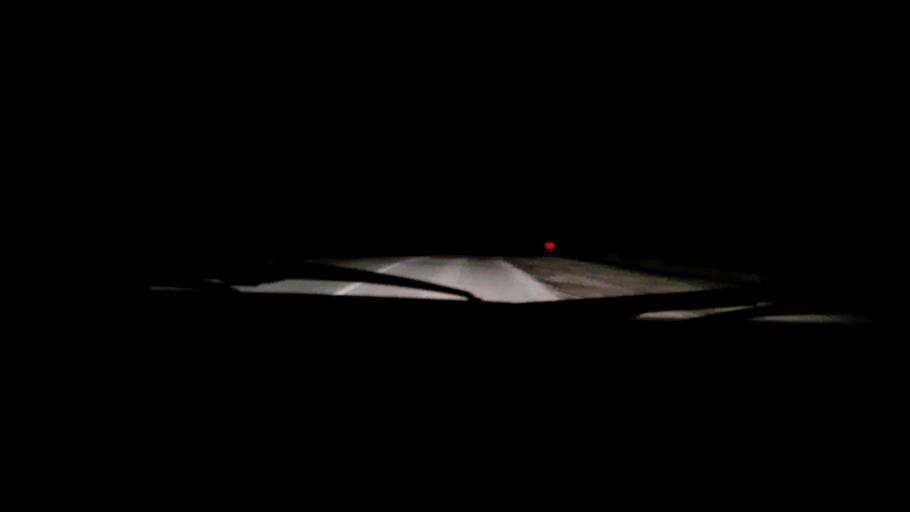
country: RU
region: Bashkortostan
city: Mikhaylovka
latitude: 54.8882
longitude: 55.8692
